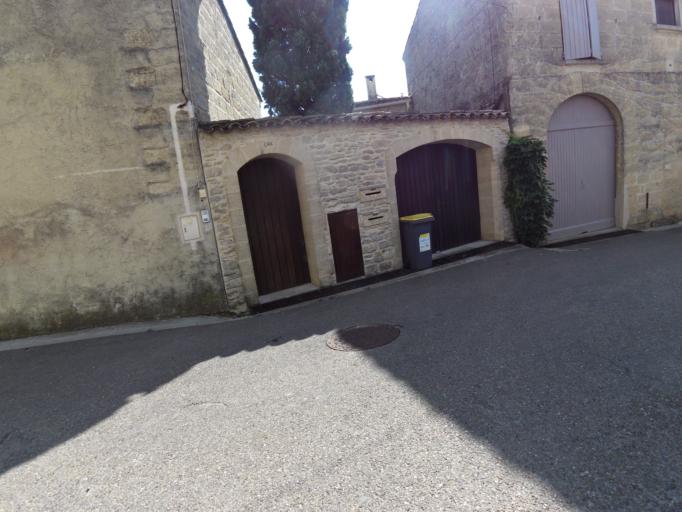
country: FR
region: Languedoc-Roussillon
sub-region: Departement du Gard
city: Gallargues-le-Montueux
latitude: 43.7225
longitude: 4.1716
